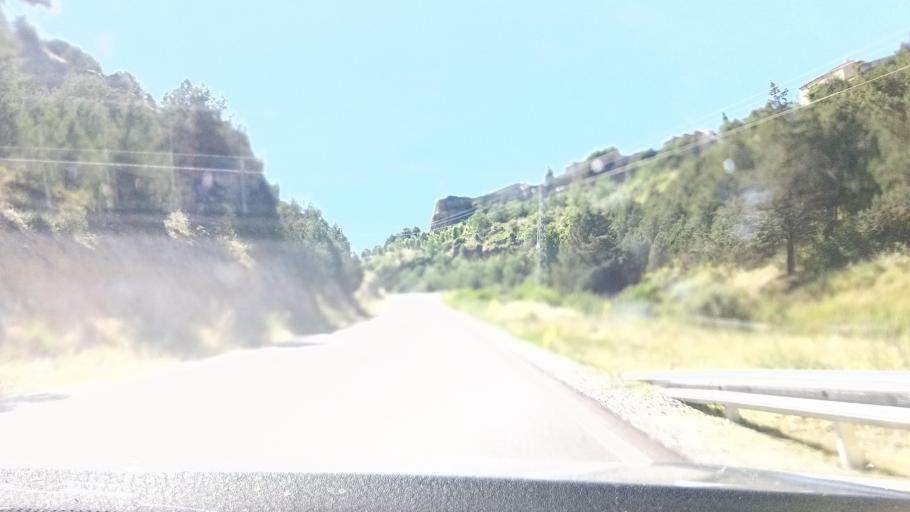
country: ES
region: Castille and Leon
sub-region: Provincia de Segovia
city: Pedraza
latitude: 41.1341
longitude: -3.8138
